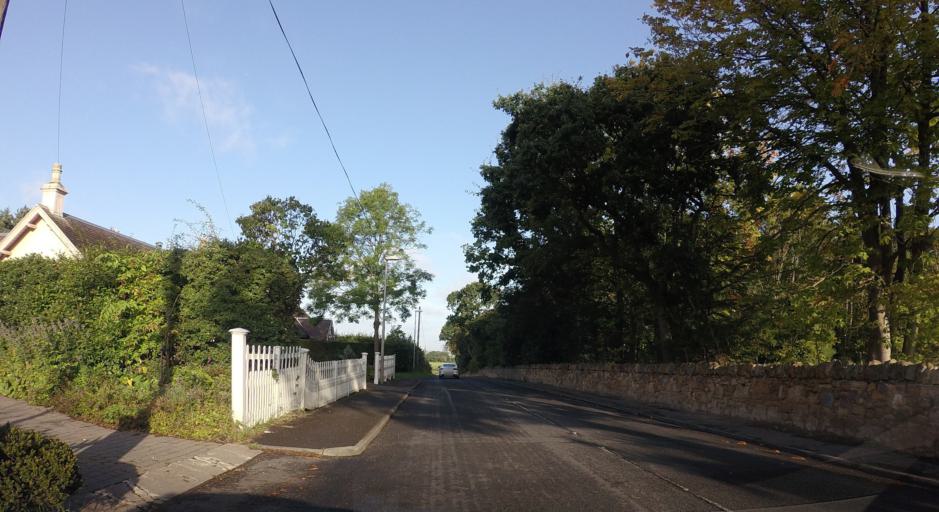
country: GB
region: Scotland
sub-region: East Lothian
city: Musselburgh
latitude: 55.9106
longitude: -3.0170
